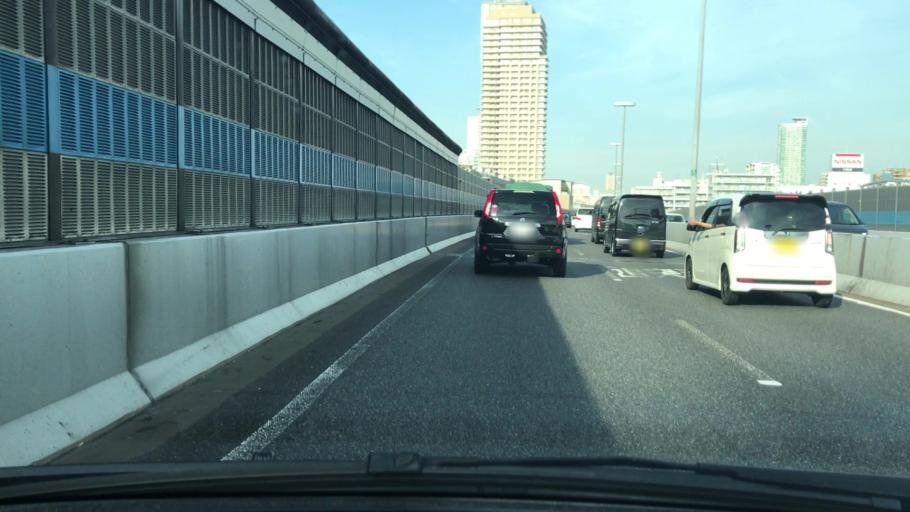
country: JP
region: Hyogo
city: Kobe
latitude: 34.7011
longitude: 135.2161
